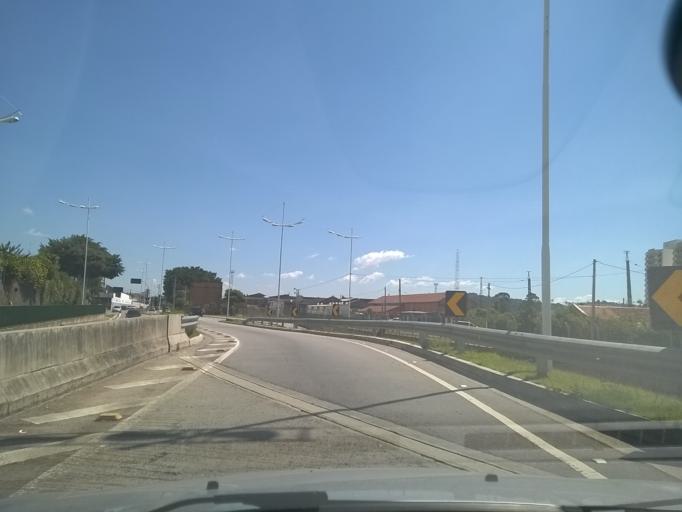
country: BR
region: Sao Paulo
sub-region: Jundiai
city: Jundiai
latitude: -23.1845
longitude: -46.8803
